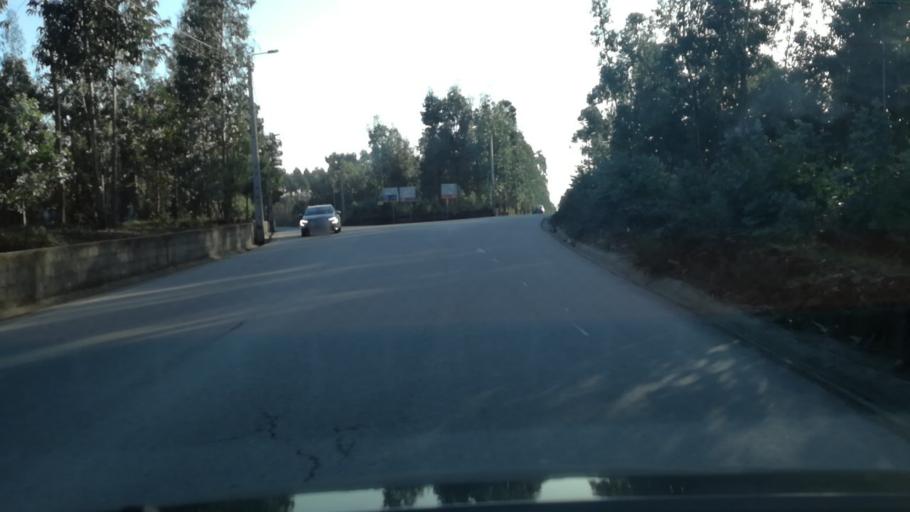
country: PT
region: Braga
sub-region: Vila Nova de Famalicao
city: Ferreiros
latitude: 41.3647
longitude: -8.5330
